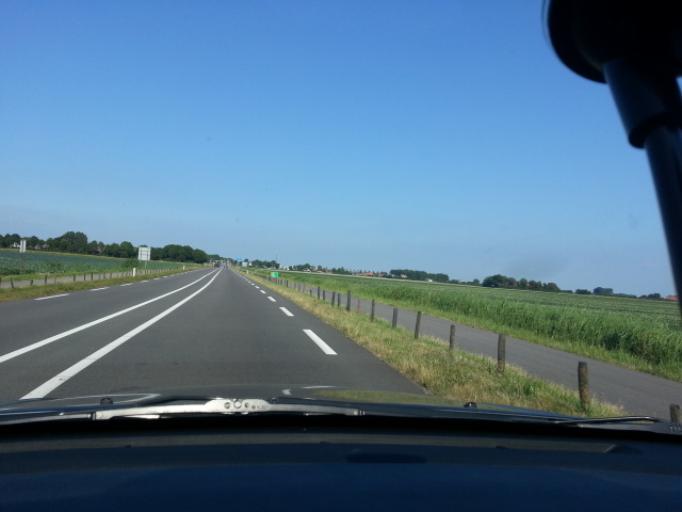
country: NL
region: Zeeland
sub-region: Schouwen-Duiveland
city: Bruinisse
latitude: 51.6440
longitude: 3.9877
